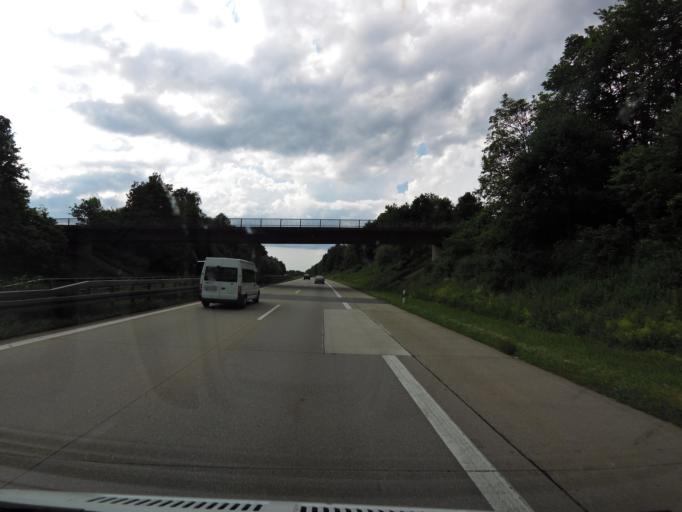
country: DE
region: Bavaria
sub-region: Lower Bavaria
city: Winzer
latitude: 48.7486
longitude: 13.0944
